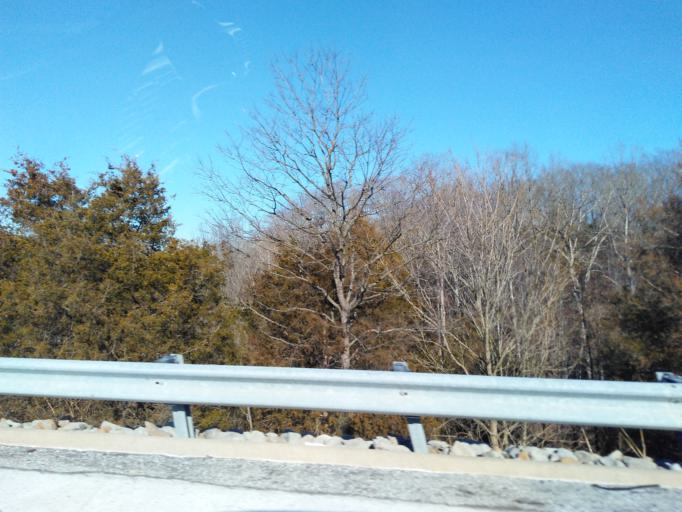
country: US
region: Illinois
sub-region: Johnson County
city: Goreville
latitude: 37.5091
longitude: -88.9048
